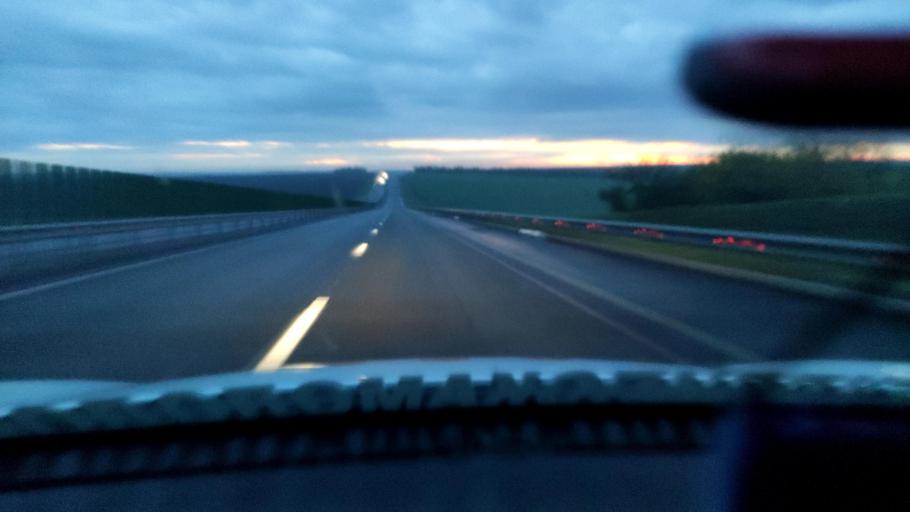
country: RU
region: Rostov
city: Tarasovskiy
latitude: 48.6801
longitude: 40.3761
